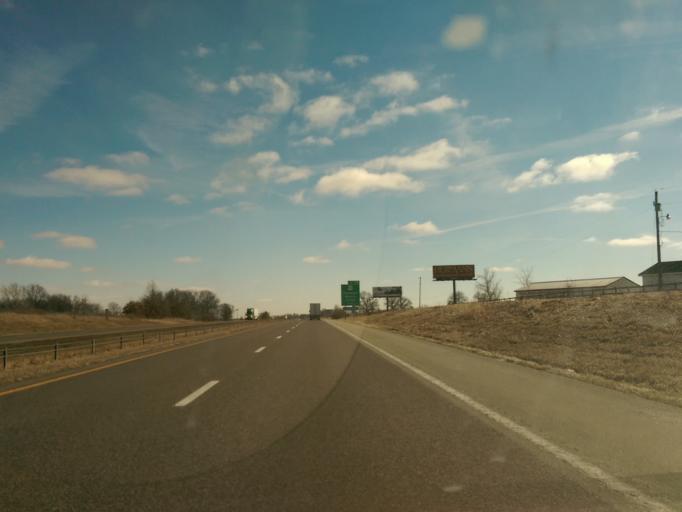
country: US
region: Missouri
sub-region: Callaway County
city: Fulton
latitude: 38.9491
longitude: -91.9605
